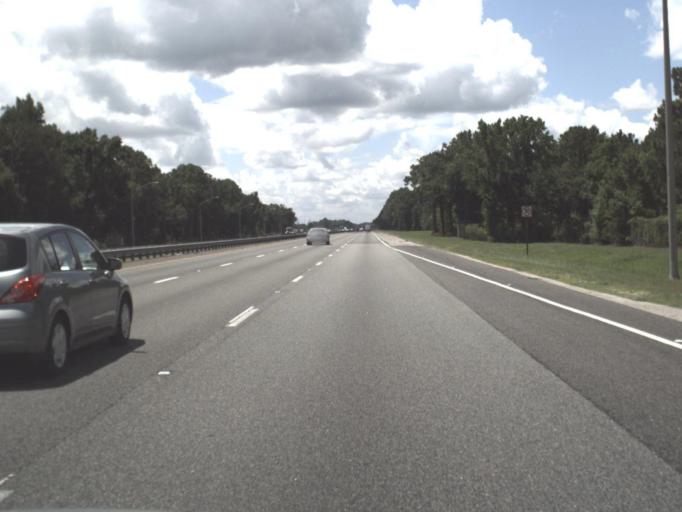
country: US
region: Florida
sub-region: Saint Johns County
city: Saint Augustine Shores
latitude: 29.7096
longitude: -81.3313
